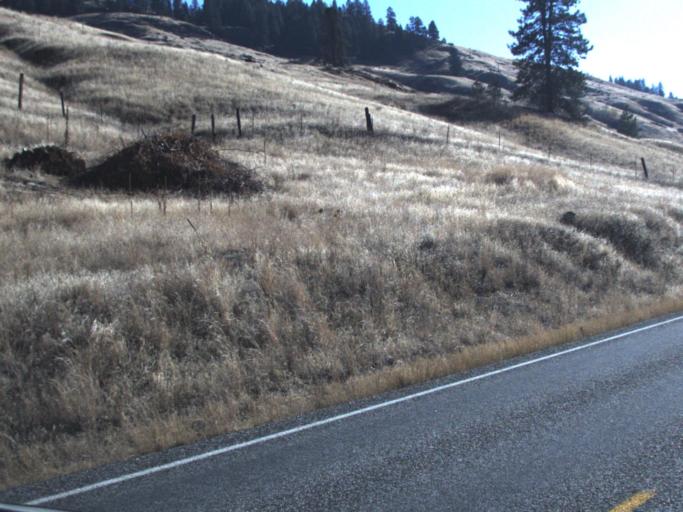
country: US
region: Washington
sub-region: Ferry County
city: Republic
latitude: 48.8475
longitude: -118.5987
